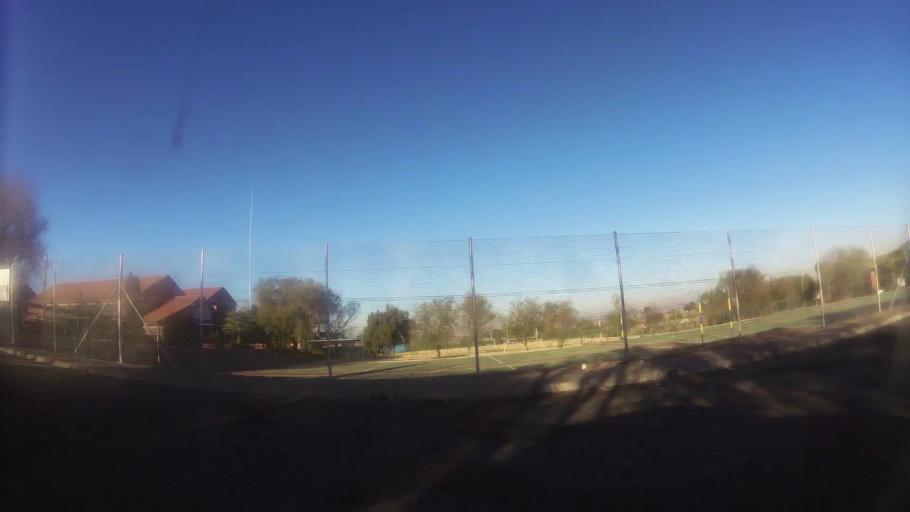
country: ZA
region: Gauteng
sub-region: City of Tshwane Metropolitan Municipality
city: Centurion
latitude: -25.8986
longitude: 28.1321
